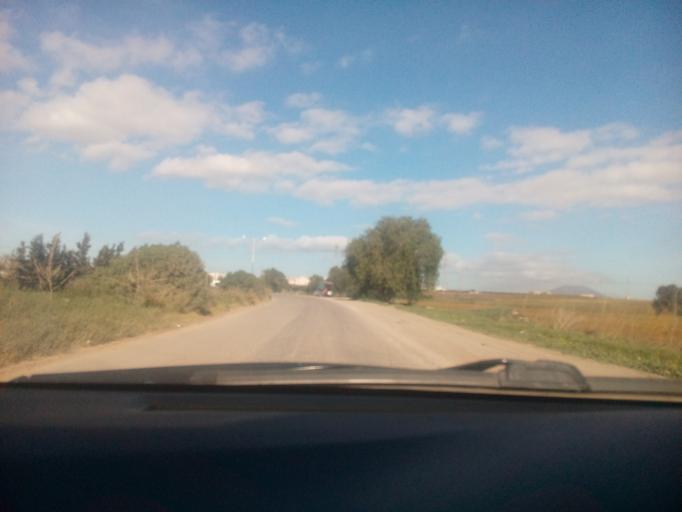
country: DZ
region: Oran
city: Sidi ech Chahmi
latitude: 35.6749
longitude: -0.5657
